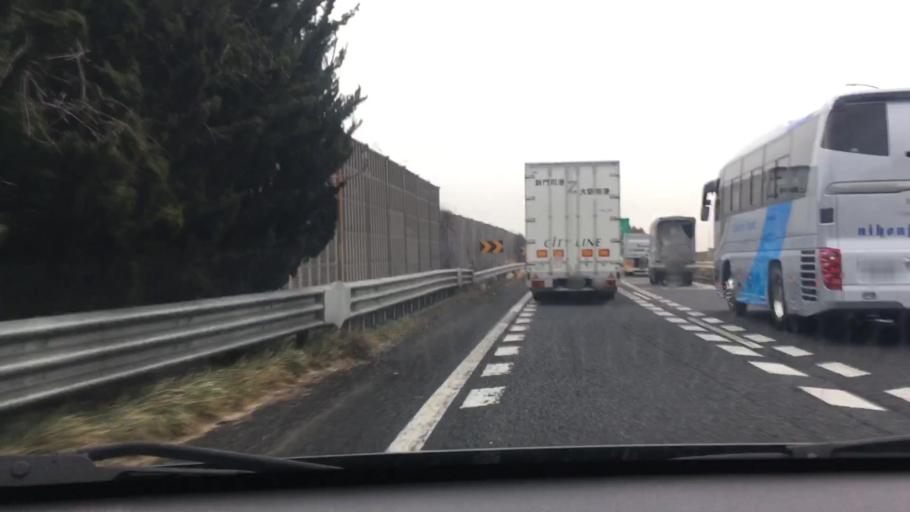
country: JP
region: Mie
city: Ueno-ebisumachi
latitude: 34.7886
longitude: 136.1606
